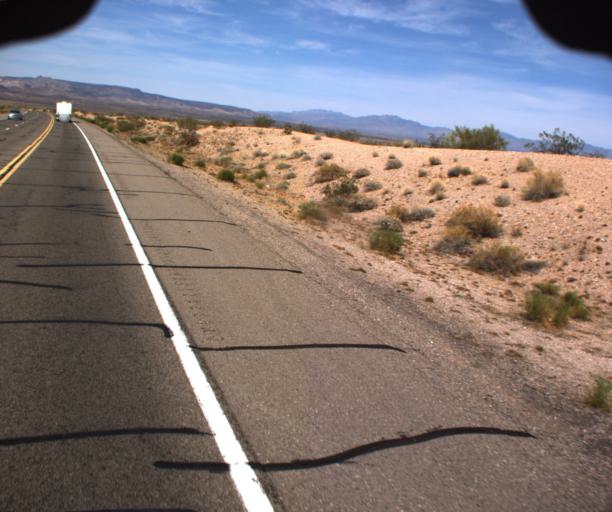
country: US
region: Arizona
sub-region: Mohave County
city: Desert Hills
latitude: 34.6860
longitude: -114.3035
